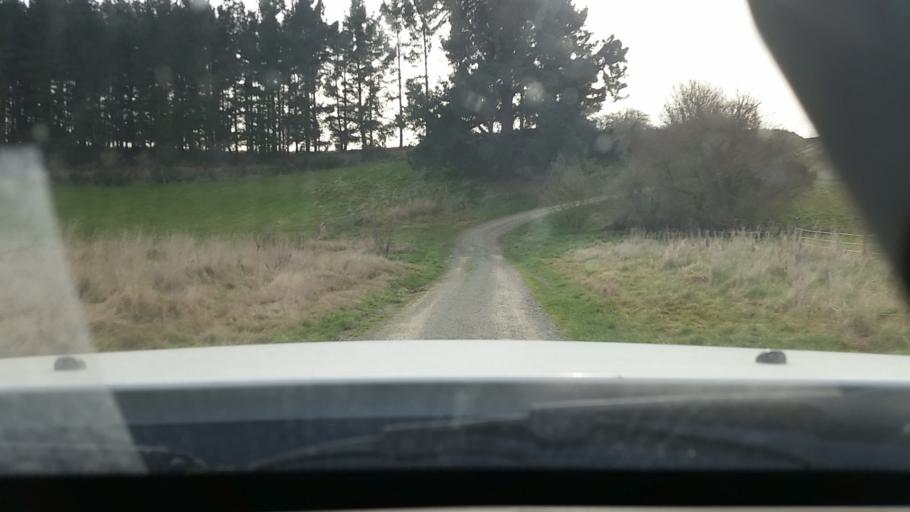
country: NZ
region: Canterbury
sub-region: Timaru District
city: Pleasant Point
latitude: -44.1966
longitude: 171.1876
